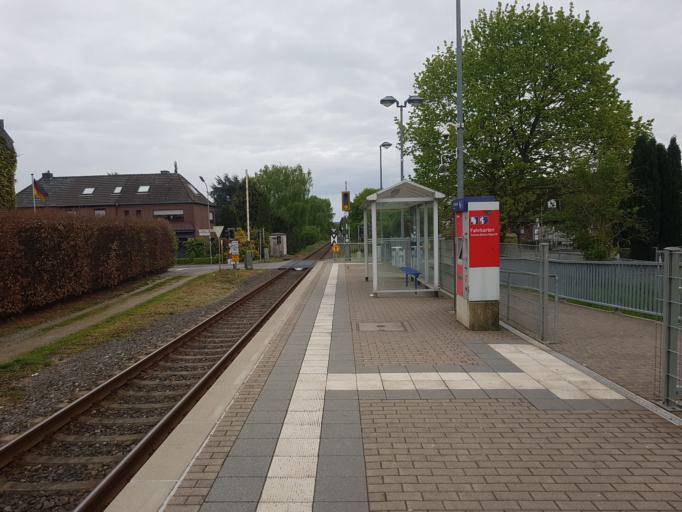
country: DE
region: North Rhine-Westphalia
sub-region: Regierungsbezirk Koln
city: Eschweiler
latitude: 50.8177
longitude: 6.2517
